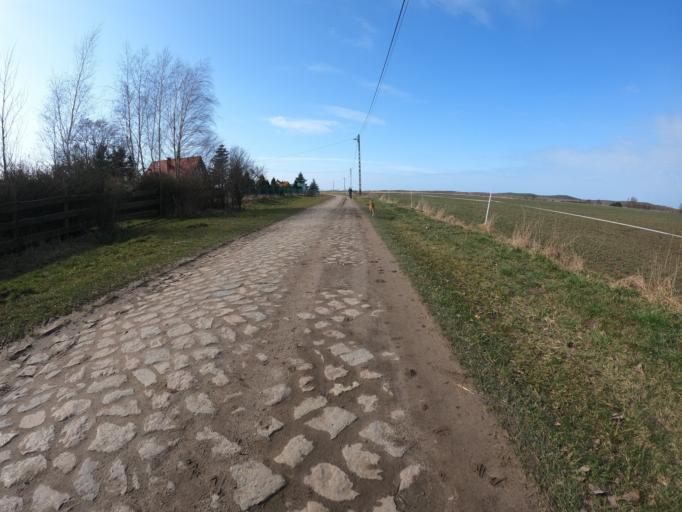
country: PL
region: West Pomeranian Voivodeship
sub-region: Powiat gryficki
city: Trzebiatow
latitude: 54.0923
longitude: 15.2070
